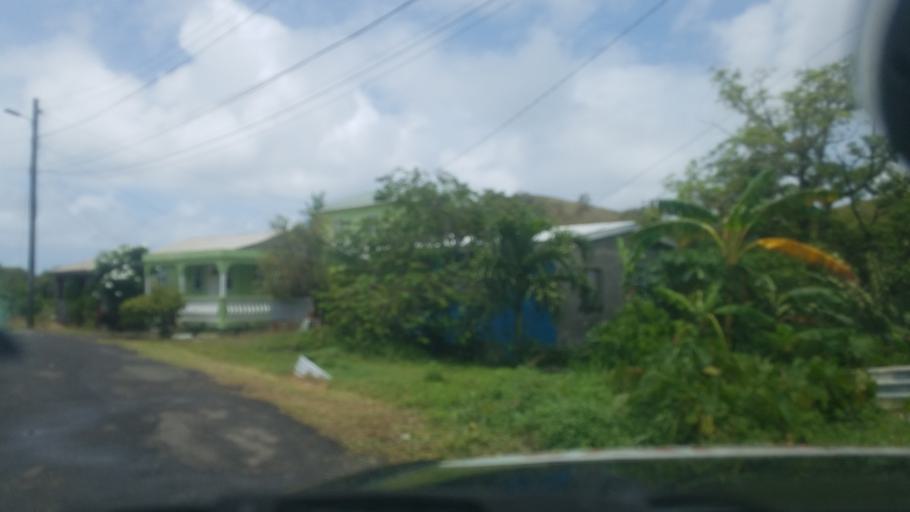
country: LC
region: Vieux-Fort
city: Vieux Fort
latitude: 13.7425
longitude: -60.9567
